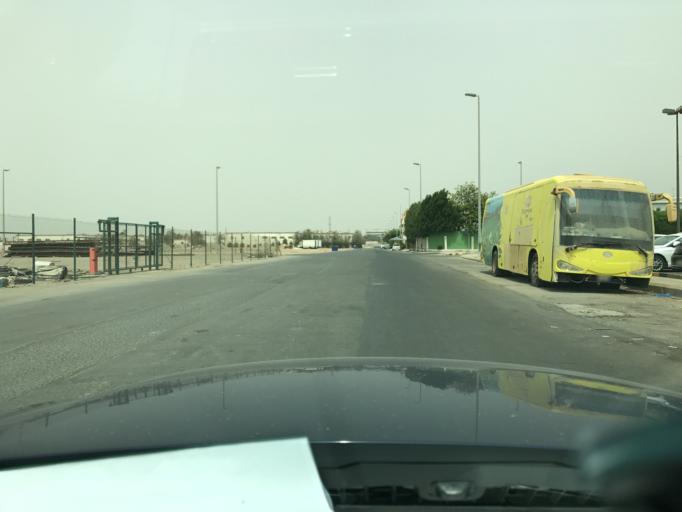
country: SA
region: Makkah
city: Jeddah
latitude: 21.5228
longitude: 39.1575
